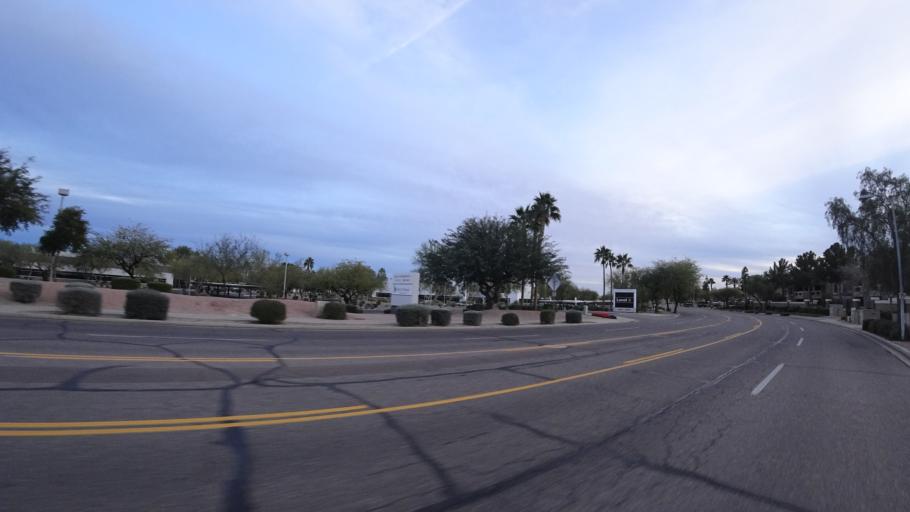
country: US
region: Arizona
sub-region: Maricopa County
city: Guadalupe
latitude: 33.3162
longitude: -111.9765
